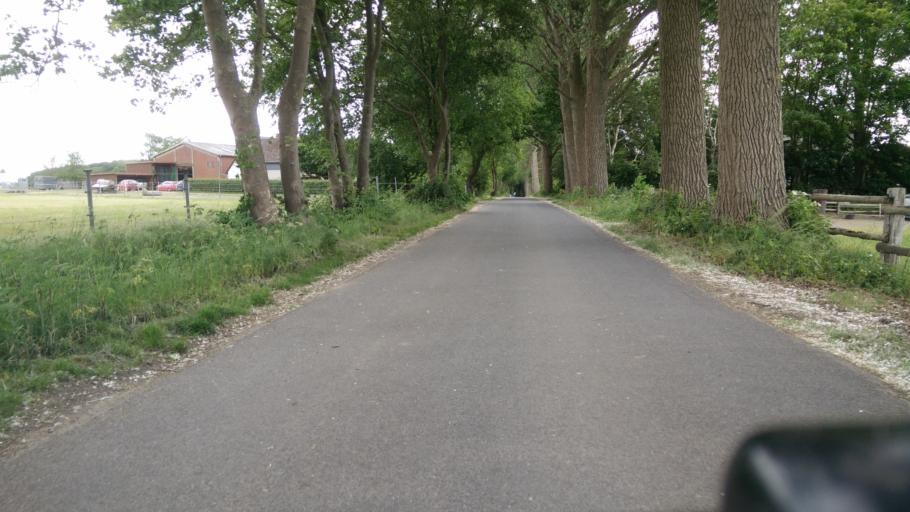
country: DE
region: Lower Saxony
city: Hagenburg
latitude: 52.4472
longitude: 9.3700
